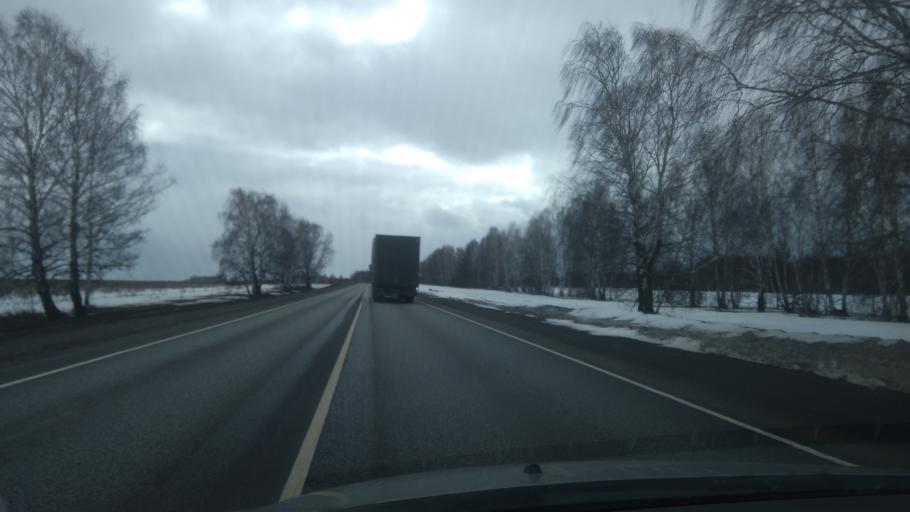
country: RU
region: Perm
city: Suksun
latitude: 56.9493
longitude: 57.5287
